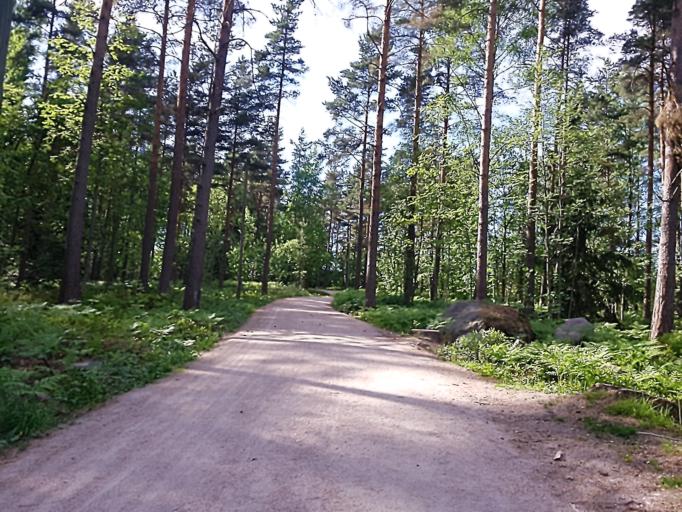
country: FI
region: Uusimaa
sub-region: Helsinki
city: Helsinki
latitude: 60.2386
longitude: 24.9567
